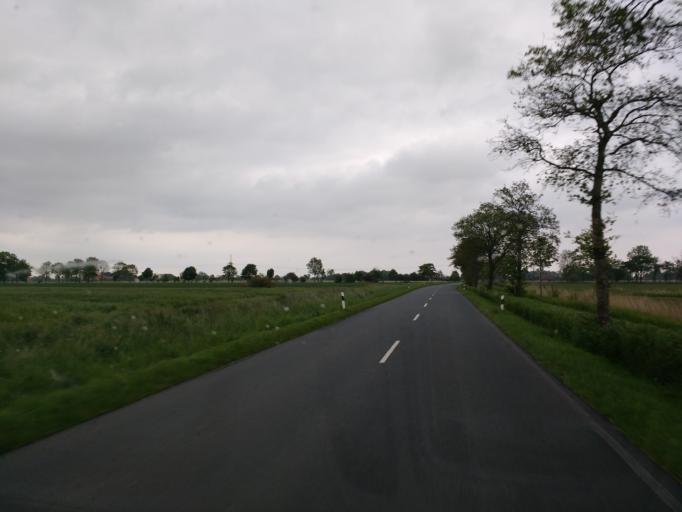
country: DE
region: Lower Saxony
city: Schillig
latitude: 53.6661
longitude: 7.9709
